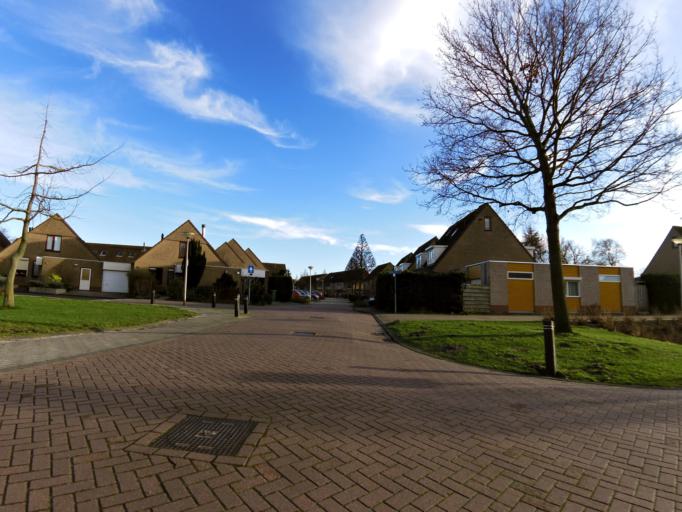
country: NL
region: South Holland
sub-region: Gemeente Brielle
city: Brielle
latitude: 51.9112
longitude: 4.1073
